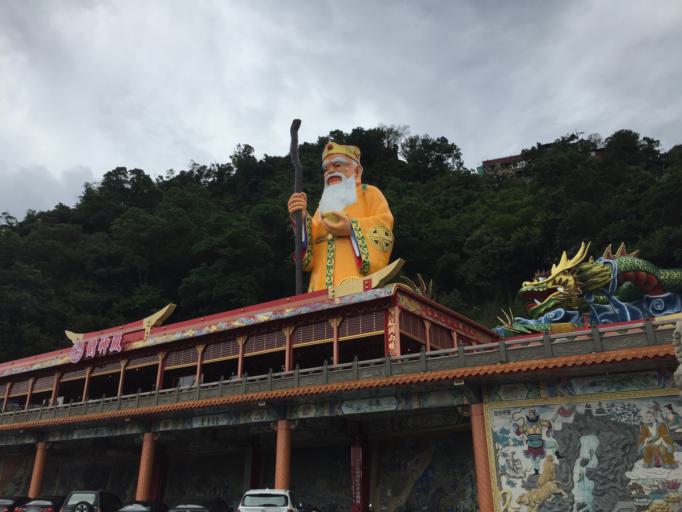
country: TW
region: Taipei
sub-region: Taipei
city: Banqiao
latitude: 24.9731
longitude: 121.4979
